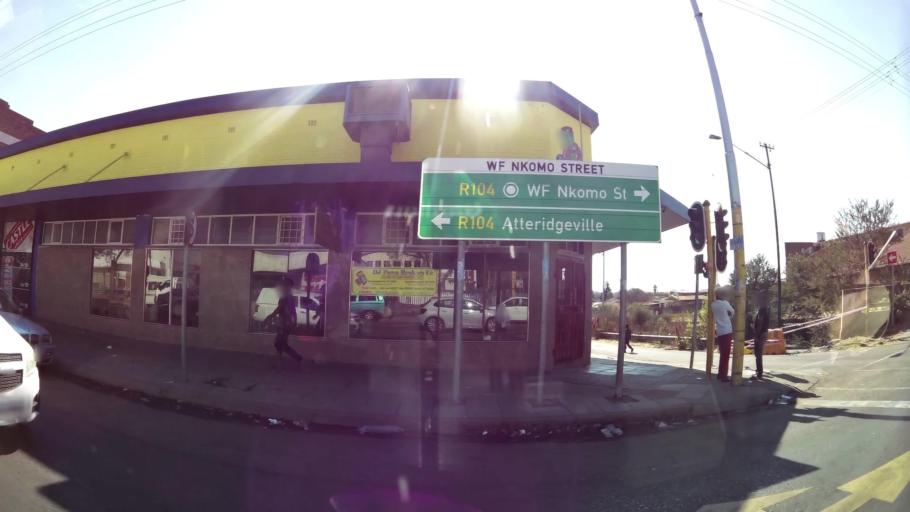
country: ZA
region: Gauteng
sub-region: City of Tshwane Metropolitan Municipality
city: Pretoria
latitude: -25.7485
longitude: 28.1572
